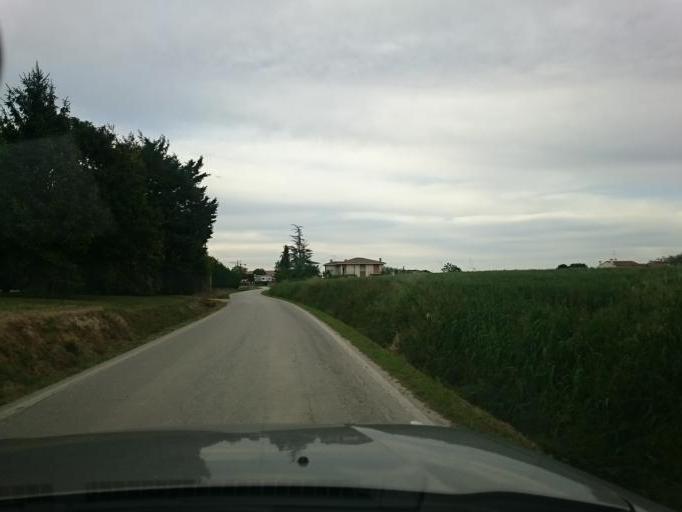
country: IT
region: Veneto
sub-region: Provincia di Padova
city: San Pietro Viminario
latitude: 45.2522
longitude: 11.8210
